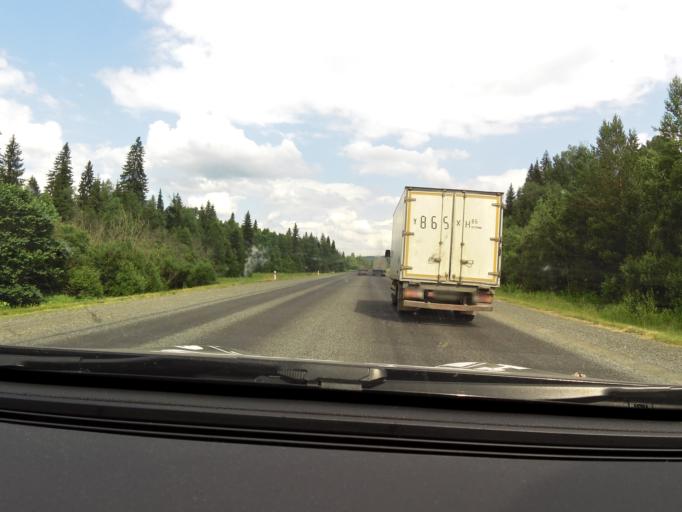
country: RU
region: Sverdlovsk
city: Arti
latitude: 56.7931
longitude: 58.4548
